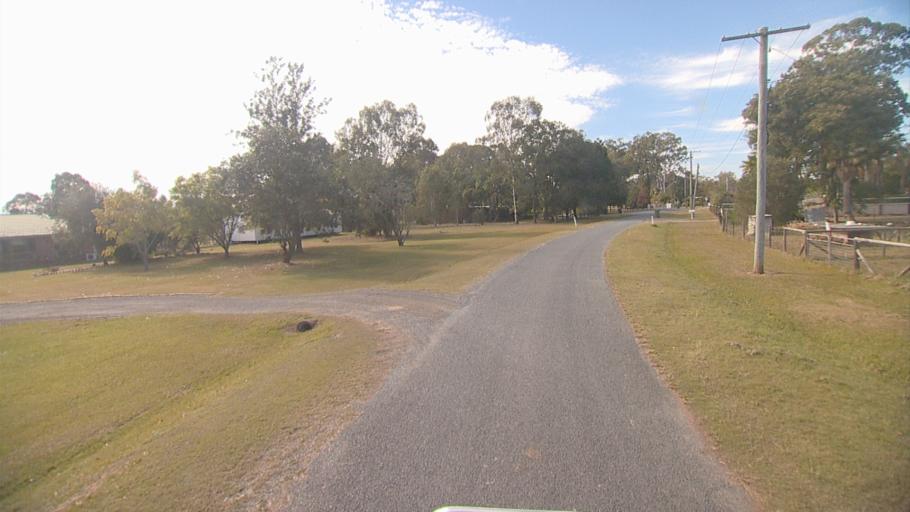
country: AU
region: Queensland
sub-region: Logan
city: North Maclean
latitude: -27.7754
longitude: 152.9971
